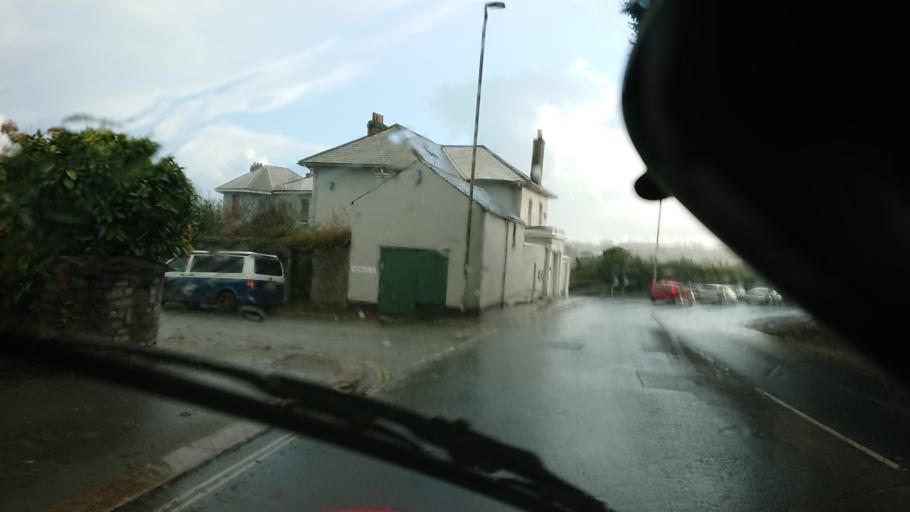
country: GB
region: England
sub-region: Cornwall
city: Millbrook
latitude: 50.3760
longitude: -4.1683
